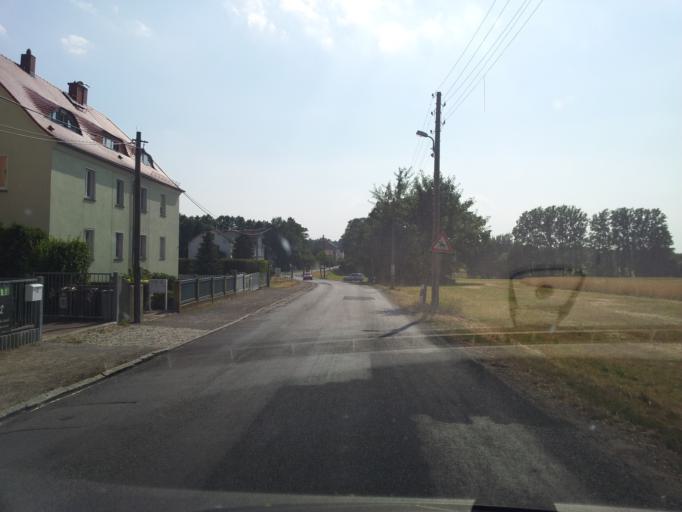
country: DE
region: Saxony
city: Ottendorf-Okrilla
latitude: 51.1308
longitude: 13.8519
